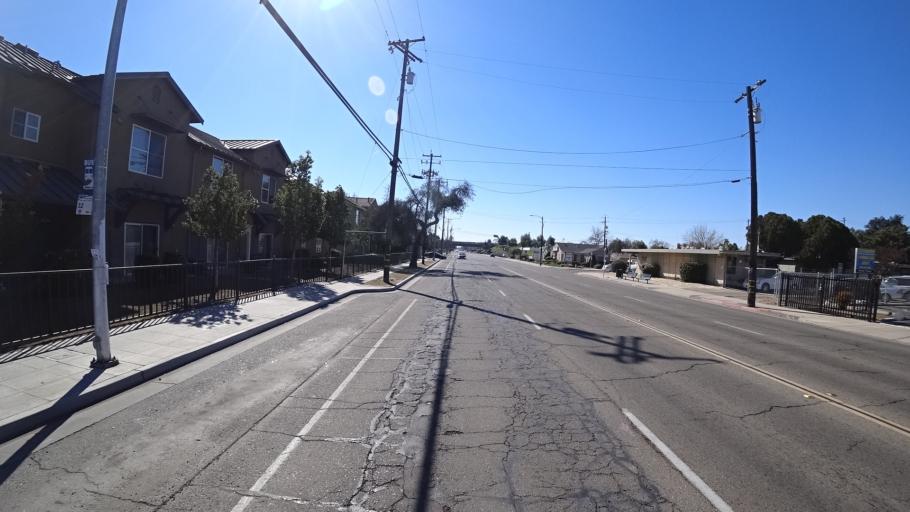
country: US
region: California
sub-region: Fresno County
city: Fresno
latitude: 36.7708
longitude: -119.7815
